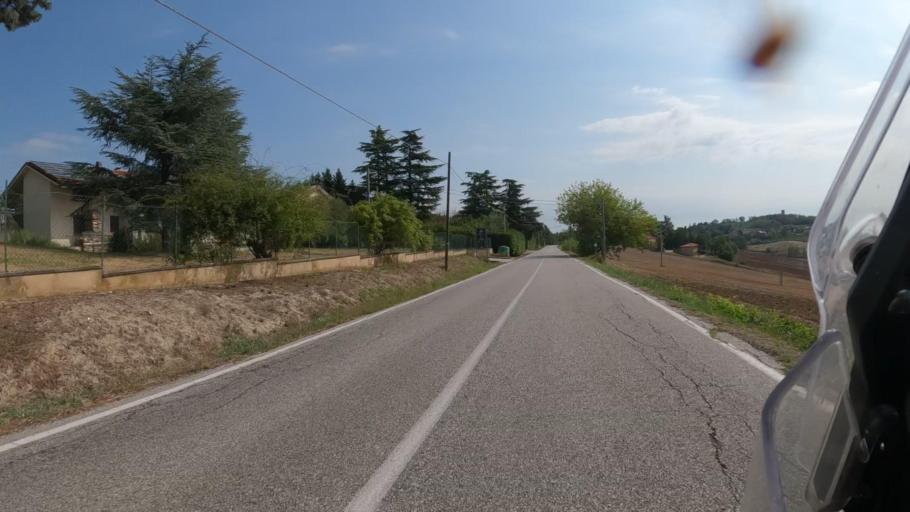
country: IT
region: Piedmont
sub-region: Provincia di Alessandria
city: San Giorgio Monferrato
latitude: 45.0915
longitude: 8.4176
